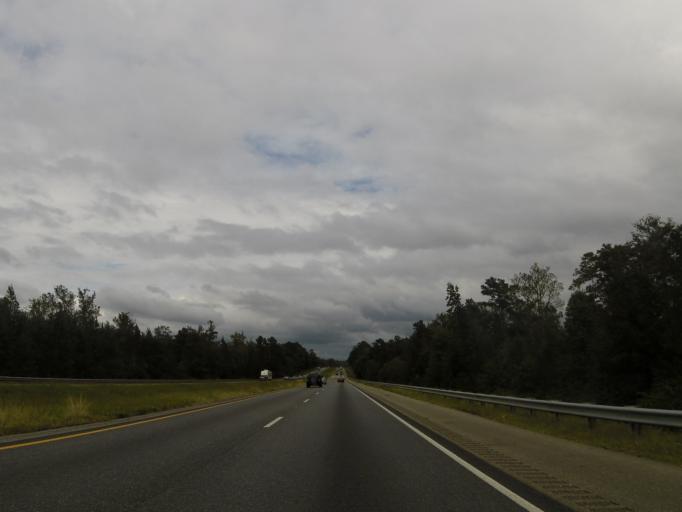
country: US
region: Alabama
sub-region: Escambia County
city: Brewton
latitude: 31.2945
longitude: -87.1811
